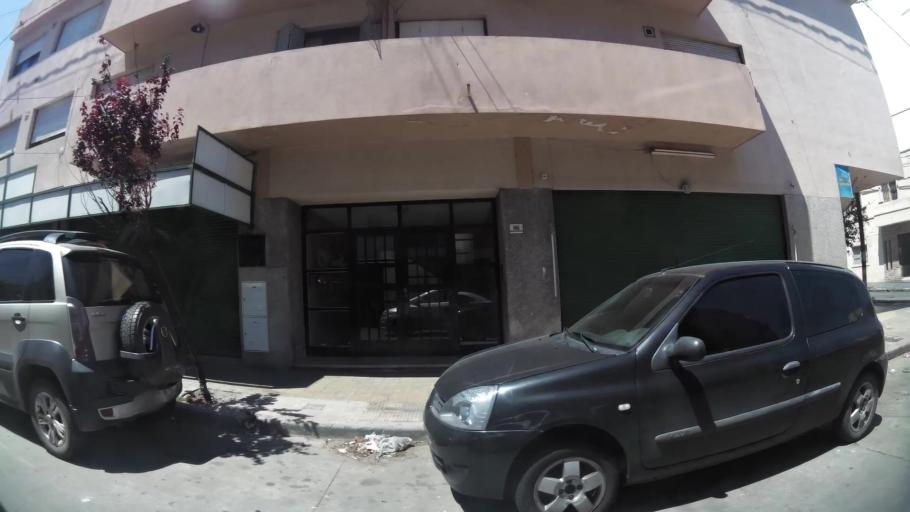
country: AR
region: Cordoba
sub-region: Departamento de Capital
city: Cordoba
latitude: -31.3973
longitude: -64.1976
